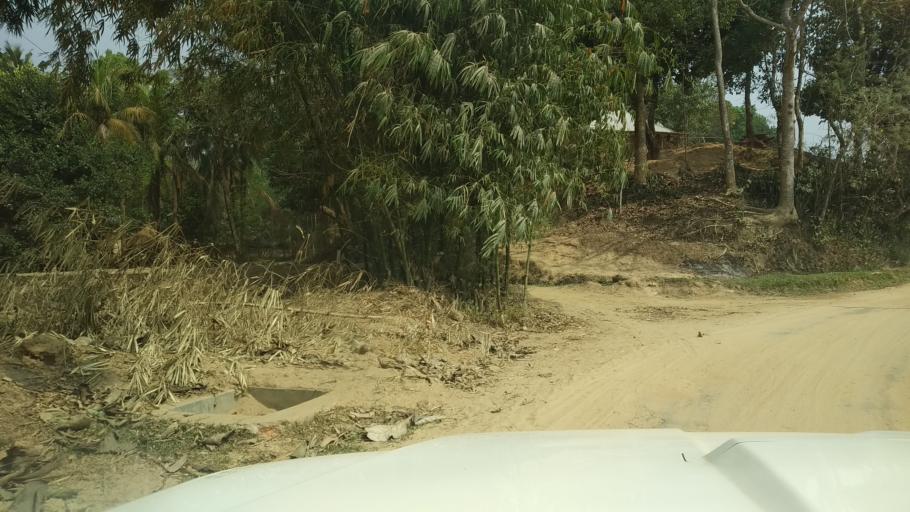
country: IN
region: Tripura
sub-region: West Tripura
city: Sonamura
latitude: 23.4270
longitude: 91.3011
